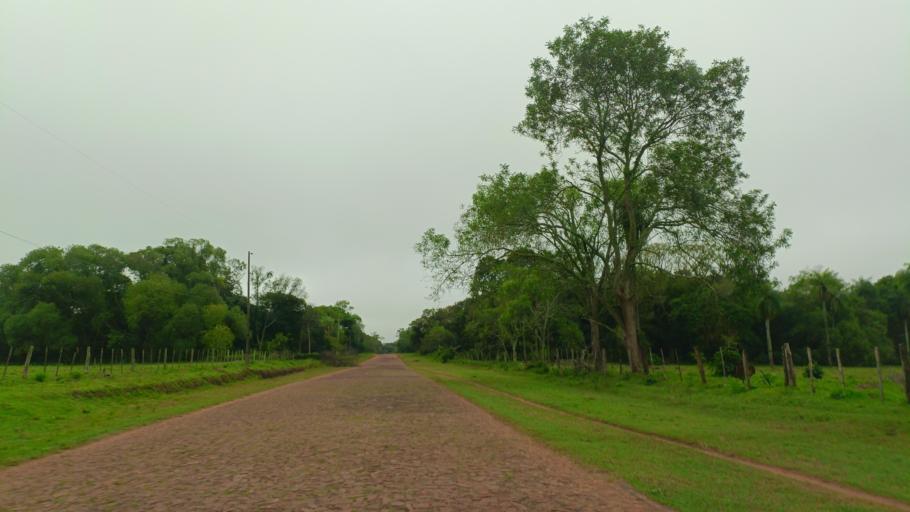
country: PY
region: Misiones
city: Santa Maria
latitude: -26.8696
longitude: -57.0116
